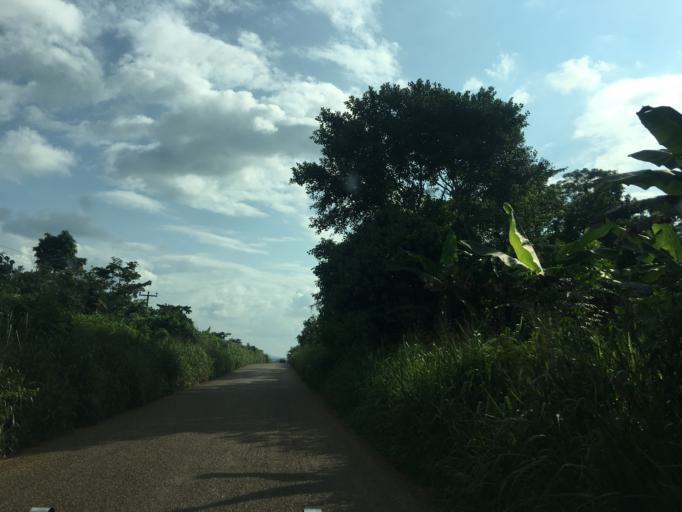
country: GH
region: Western
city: Bibiani
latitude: 6.7715
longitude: -2.5672
